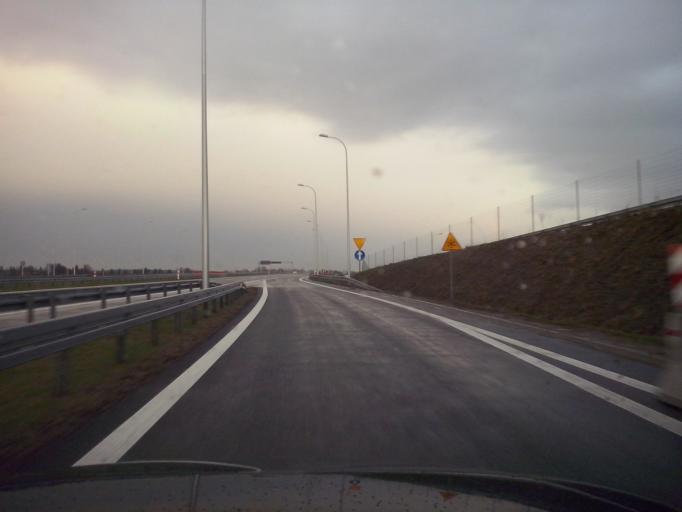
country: PL
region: Lublin Voivodeship
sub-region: Powiat lubelski
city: Jastkow
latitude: 51.2814
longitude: 22.4595
